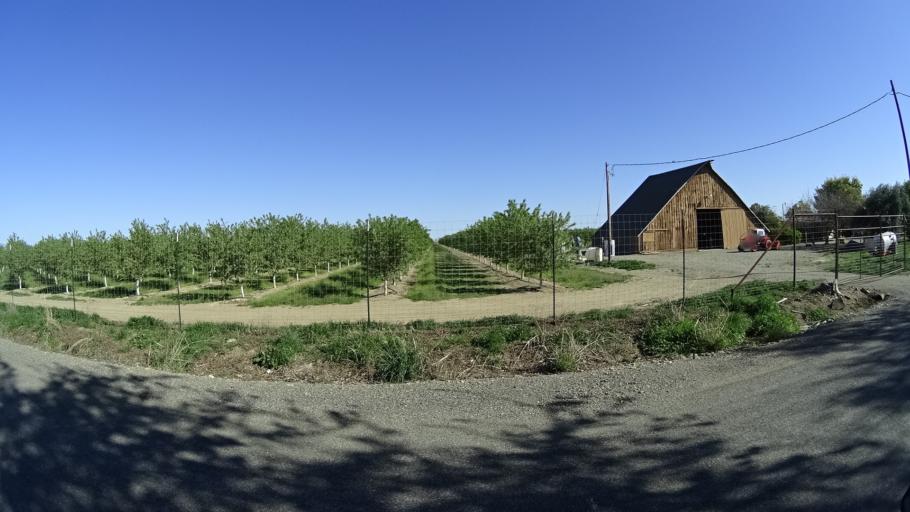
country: US
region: California
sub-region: Glenn County
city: Orland
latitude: 39.7477
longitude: -122.2225
